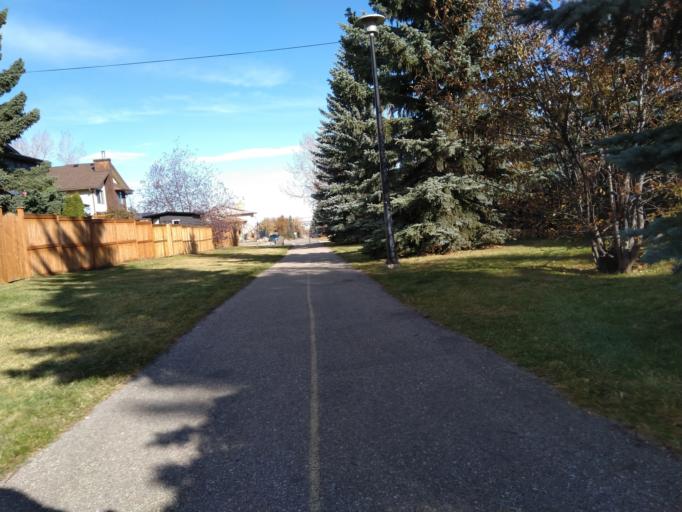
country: CA
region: Alberta
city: Calgary
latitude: 51.1265
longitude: -114.0857
